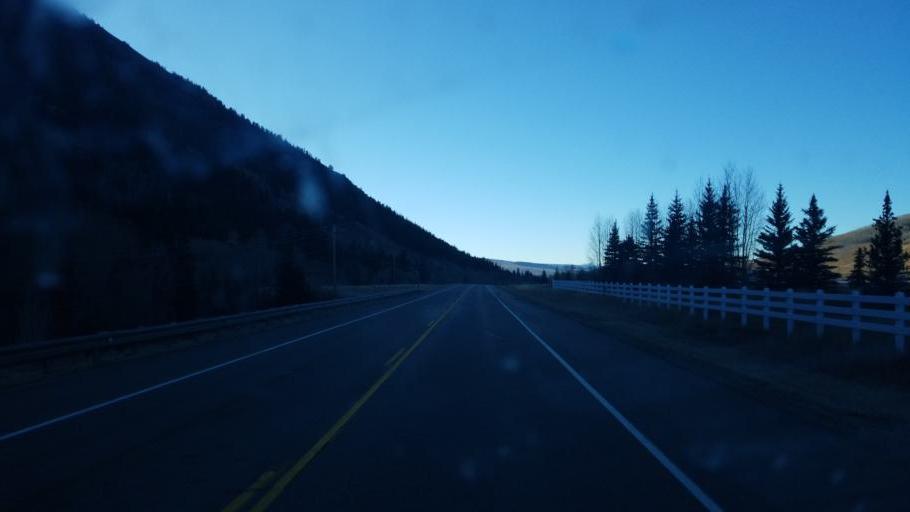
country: US
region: Colorado
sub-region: Gunnison County
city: Crested Butte
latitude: 38.7894
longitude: -106.8735
